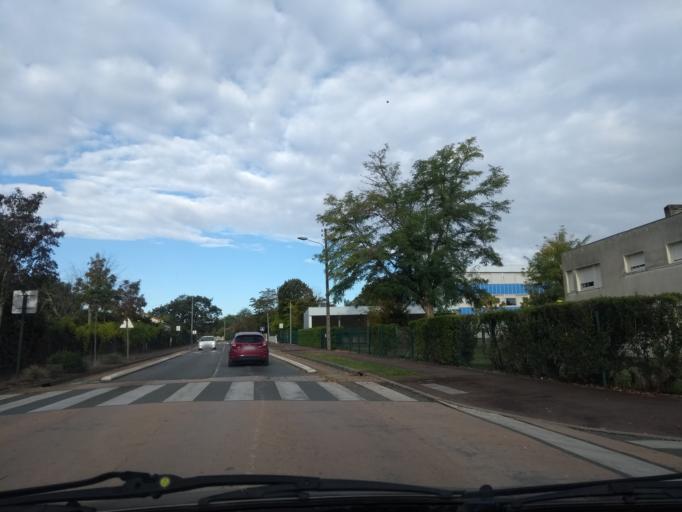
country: FR
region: Aquitaine
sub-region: Departement de la Gironde
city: Gradignan
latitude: 44.7792
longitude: -0.6112
